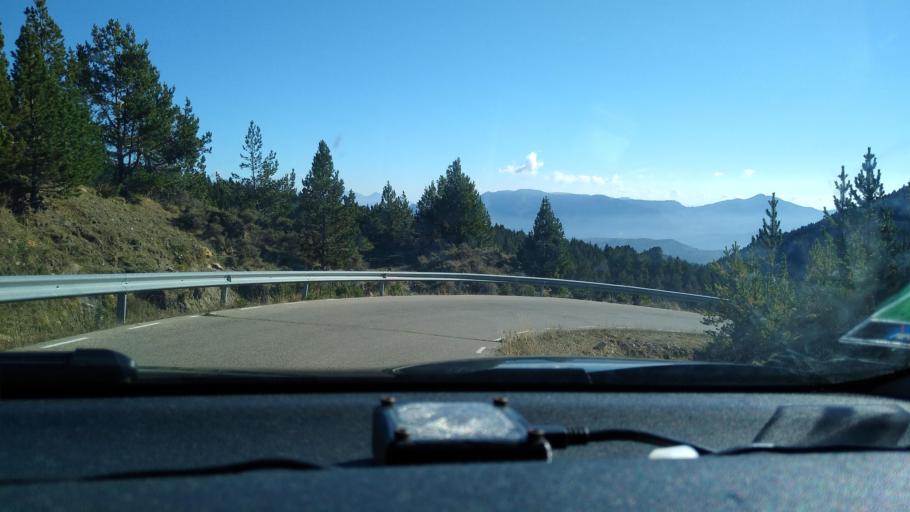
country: ES
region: Catalonia
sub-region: Provincia de Barcelona
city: Vallcebre
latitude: 42.2019
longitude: 1.7727
